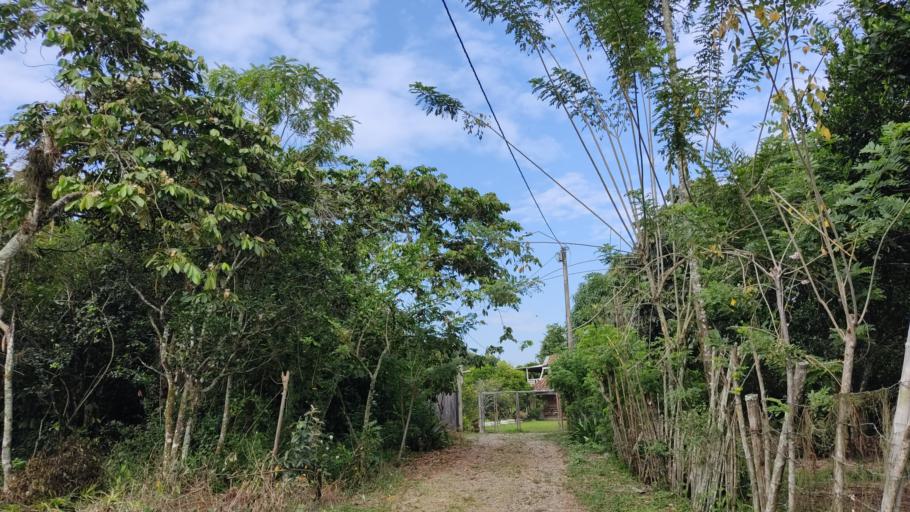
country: CO
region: Valle del Cauca
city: Jamundi
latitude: 3.1259
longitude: -76.5576
